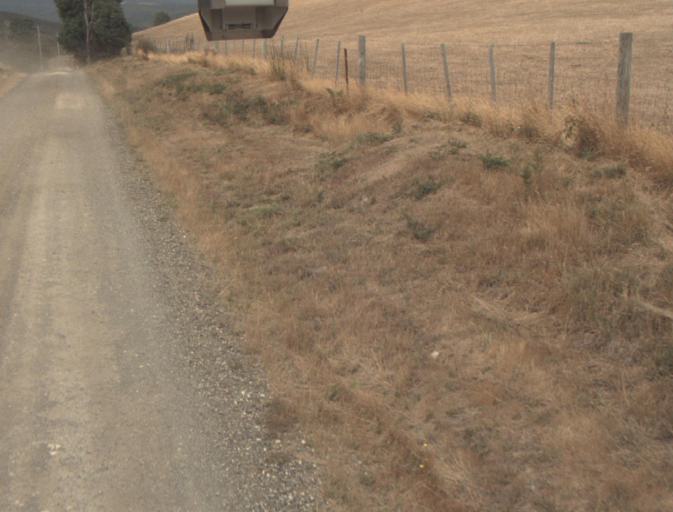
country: AU
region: Tasmania
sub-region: Dorset
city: Bridport
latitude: -41.1831
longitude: 147.2617
